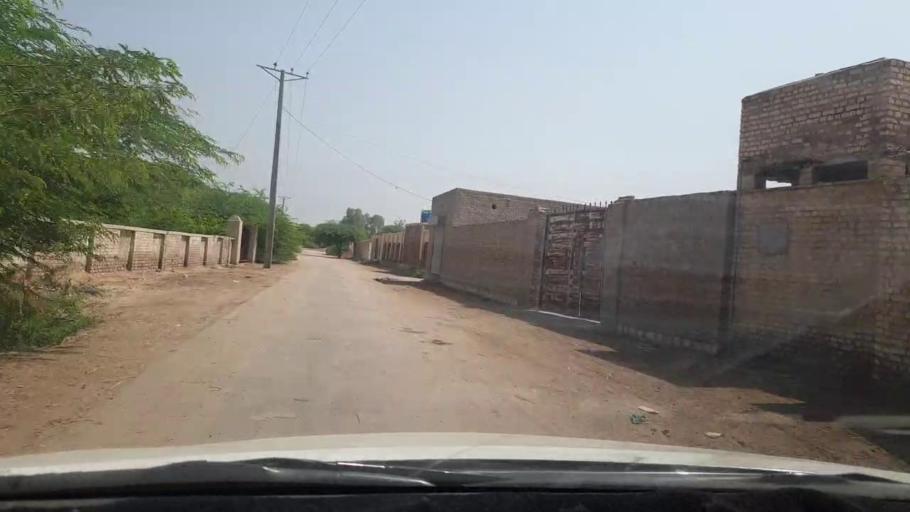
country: PK
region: Sindh
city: Rohri
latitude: 27.6010
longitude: 68.9069
